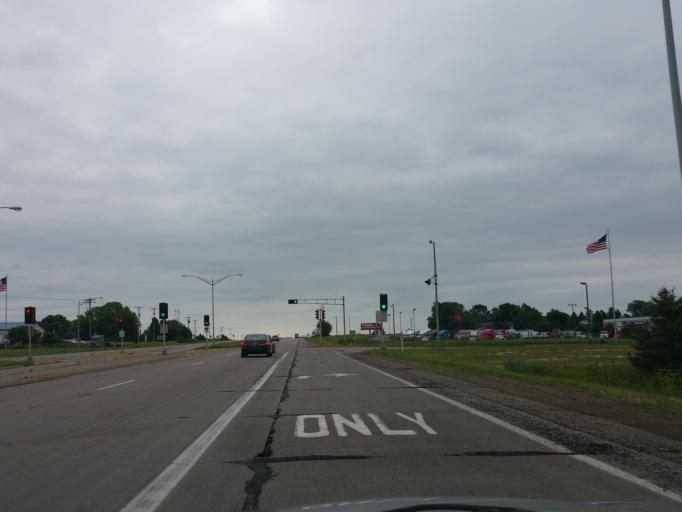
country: US
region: Wisconsin
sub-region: Eau Claire County
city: Eau Claire
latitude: 44.8434
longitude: -91.5950
